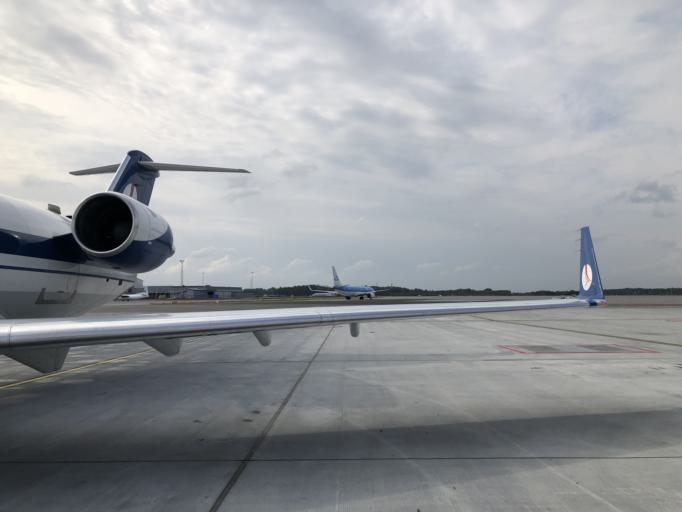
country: SE
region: Stockholm
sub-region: Sigtuna Kommun
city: Rosersberg
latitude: 59.6427
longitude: 17.9321
